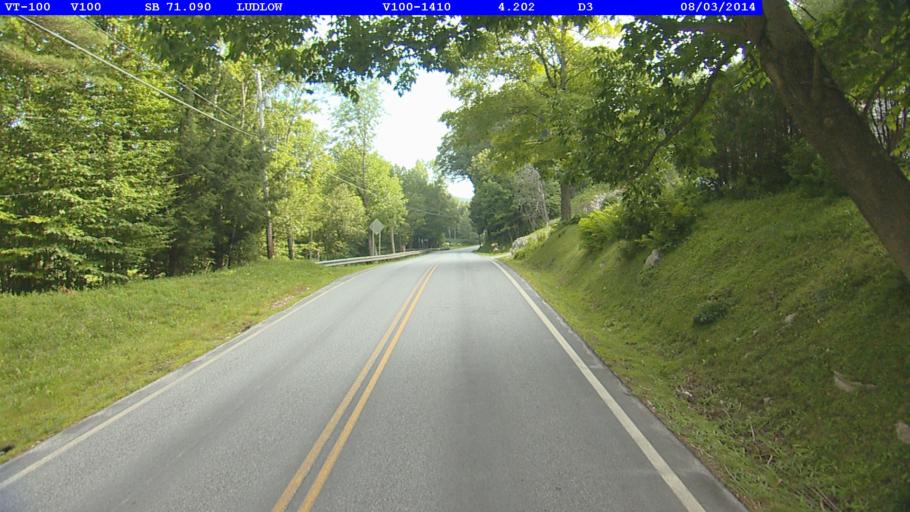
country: US
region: Vermont
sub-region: Windsor County
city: Chester
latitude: 43.3857
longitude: -72.7099
